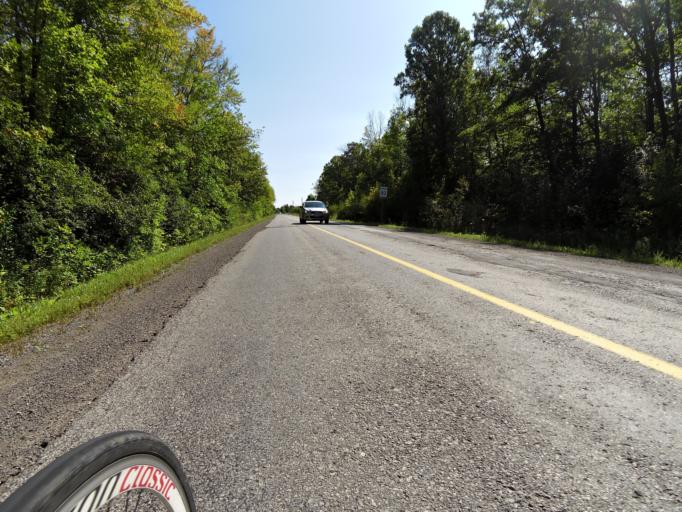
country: CA
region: Ontario
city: Bells Corners
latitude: 45.4333
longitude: -76.0611
